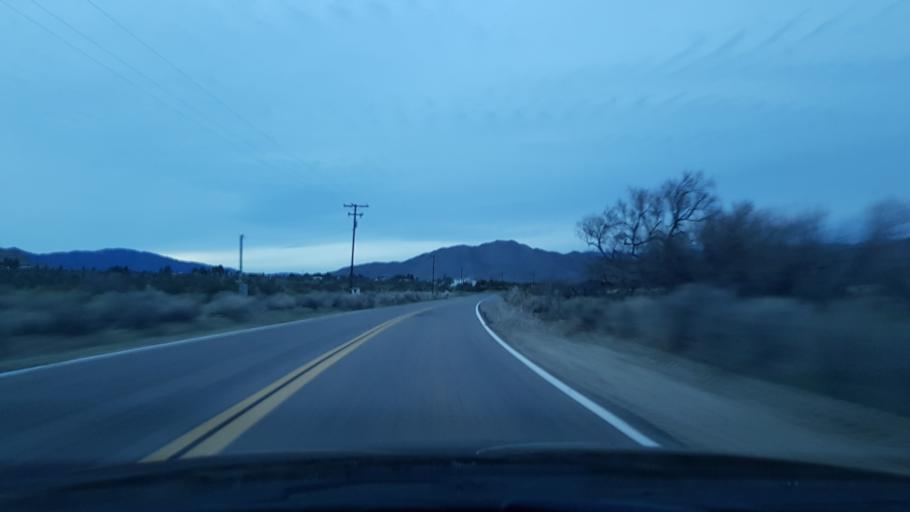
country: US
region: California
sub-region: San Diego County
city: Julian
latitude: 33.0615
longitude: -116.4255
